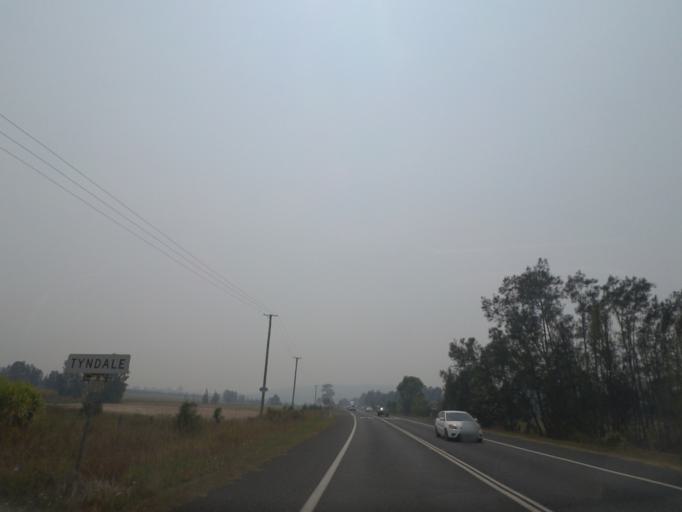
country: AU
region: New South Wales
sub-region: Clarence Valley
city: Maclean
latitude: -29.5667
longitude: 153.1350
